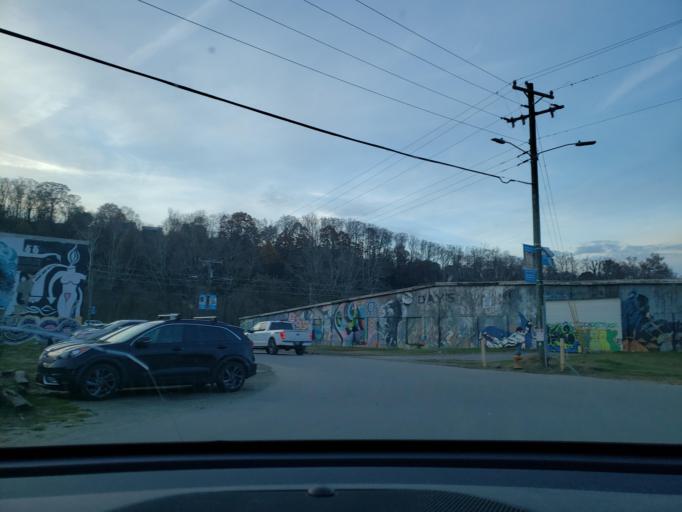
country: US
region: North Carolina
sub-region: Buncombe County
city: Asheville
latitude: 35.5778
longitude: -82.5665
